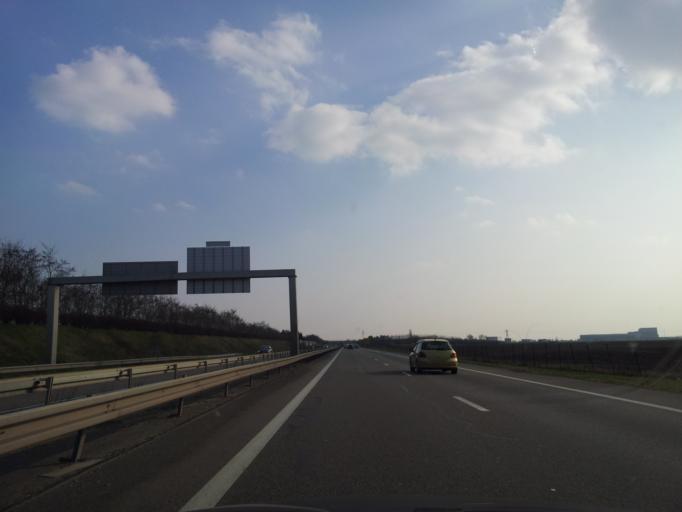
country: FR
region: Alsace
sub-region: Departement du Haut-Rhin
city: Sainte-Croix-en-Plaine
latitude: 48.0099
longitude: 7.3765
